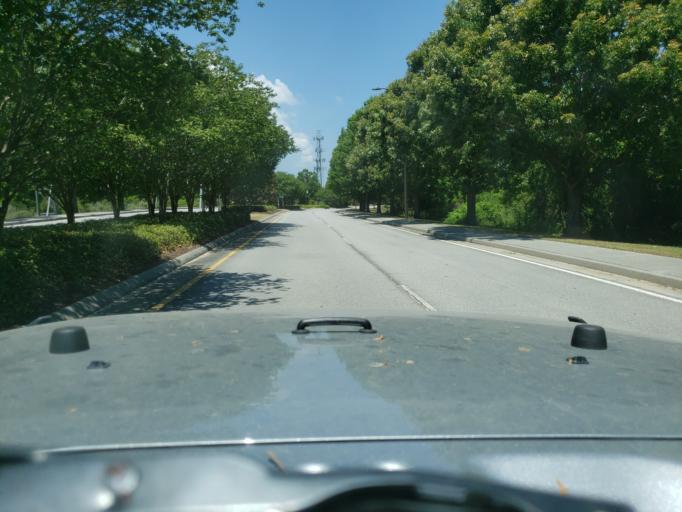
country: US
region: Georgia
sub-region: Chatham County
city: Savannah
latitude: 32.0895
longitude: -81.0878
